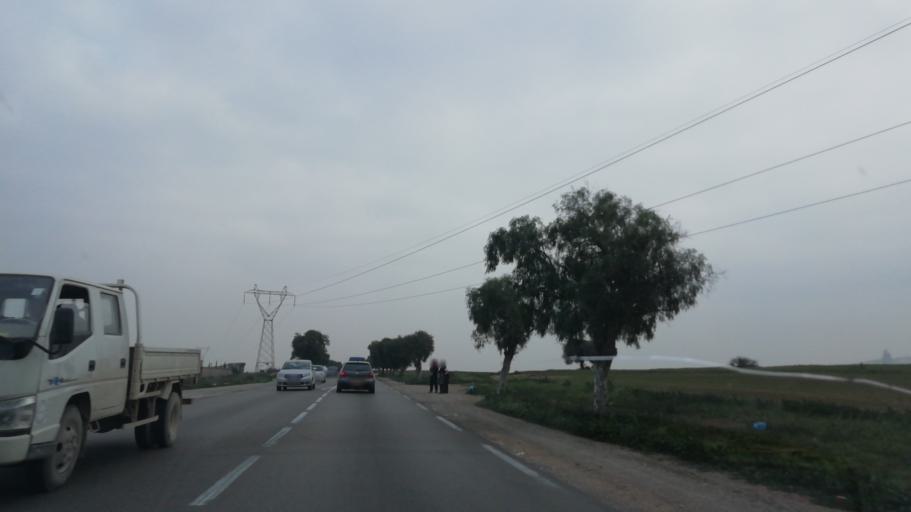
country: DZ
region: Mascara
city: Sig
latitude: 35.5453
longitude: -0.3047
